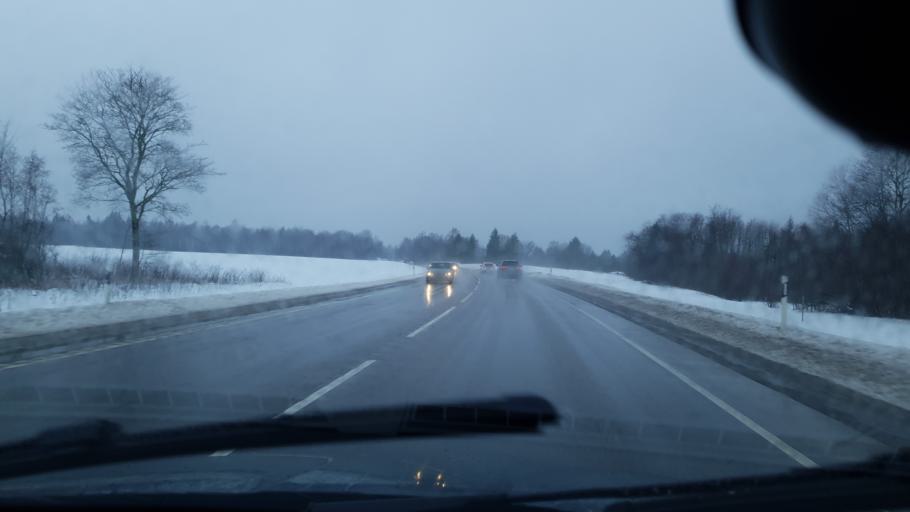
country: EE
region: Harju
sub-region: Anija vald
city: Kehra
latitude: 59.1645
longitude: 25.2450
